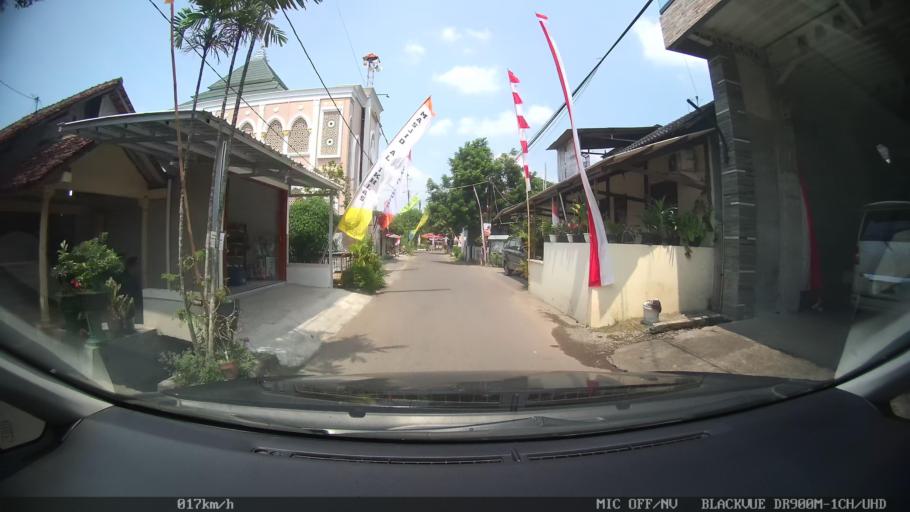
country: ID
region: Daerah Istimewa Yogyakarta
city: Yogyakarta
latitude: -7.8067
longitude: 110.4001
